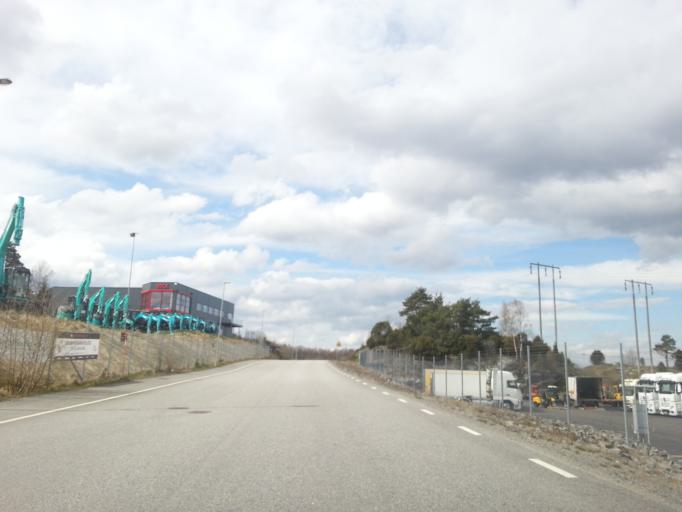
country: SE
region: Vaestra Goetaland
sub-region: Kungalvs Kommun
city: Kungalv
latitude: 57.8832
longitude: 11.9406
